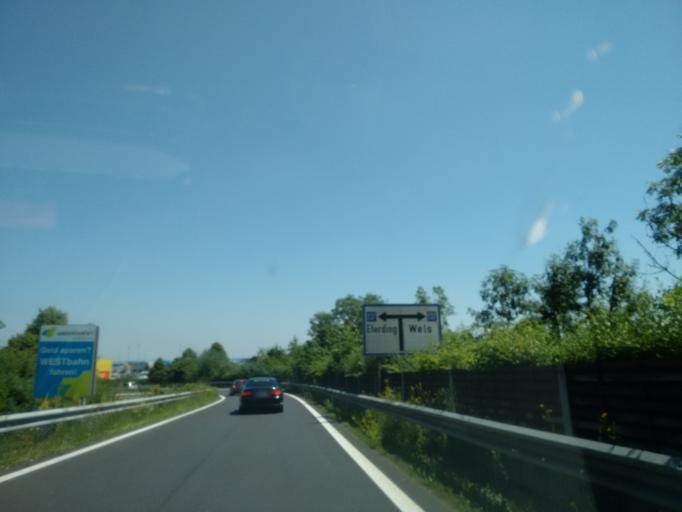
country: AT
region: Upper Austria
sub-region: Wels Stadt
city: Wels
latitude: 48.1844
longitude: 14.0217
